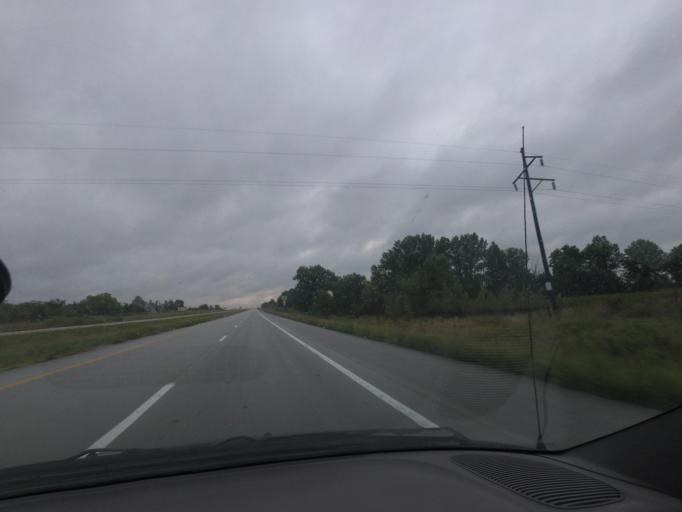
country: US
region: Missouri
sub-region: Marion County
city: Monroe City
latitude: 39.6636
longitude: -91.7074
